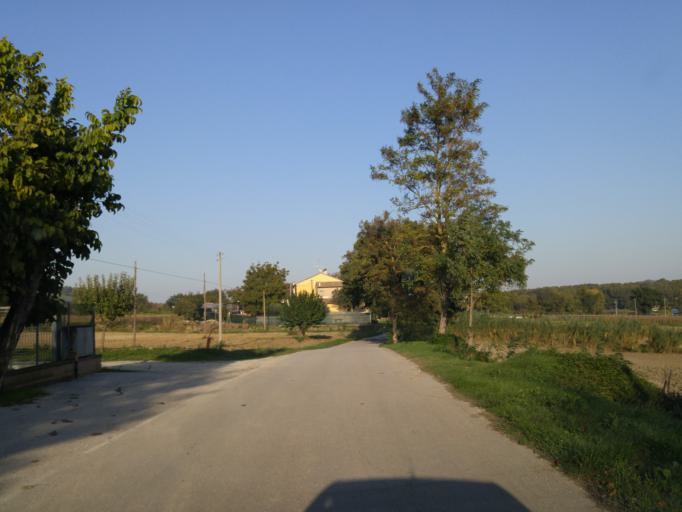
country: IT
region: The Marches
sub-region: Provincia di Pesaro e Urbino
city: Tavernelle
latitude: 43.7185
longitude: 12.8681
